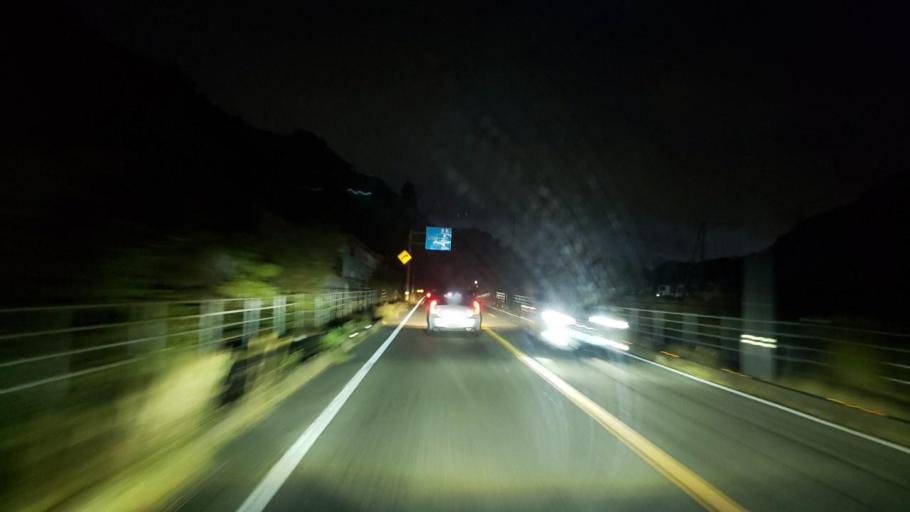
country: JP
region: Tokushima
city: Narutocho-mitsuishi
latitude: 34.2101
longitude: 134.5618
